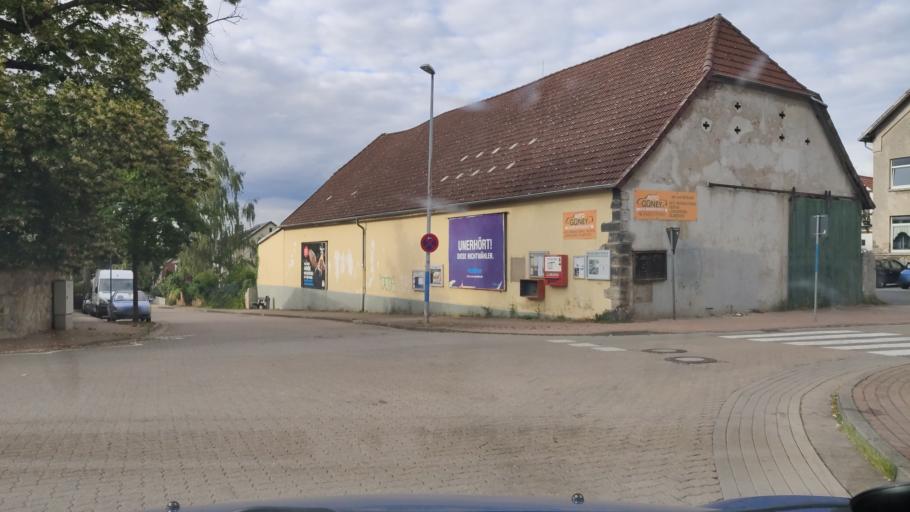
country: DE
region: Lower Saxony
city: Ronnenberg
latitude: 52.3178
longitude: 9.6548
